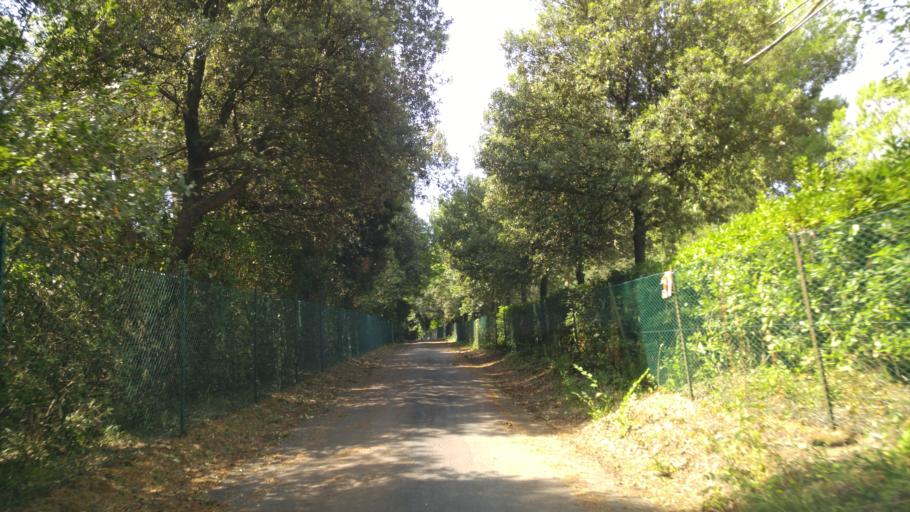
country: IT
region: The Marches
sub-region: Provincia di Pesaro e Urbino
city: Centinarola
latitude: 43.8519
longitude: 12.9918
